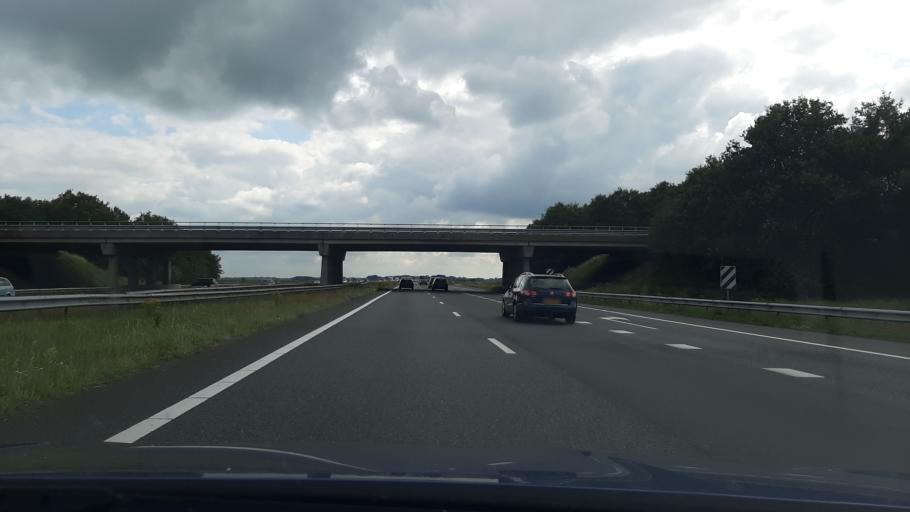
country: NL
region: Friesland
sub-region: Gemeente Smallingerland
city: Boornbergum
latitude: 53.0641
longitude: 6.0542
